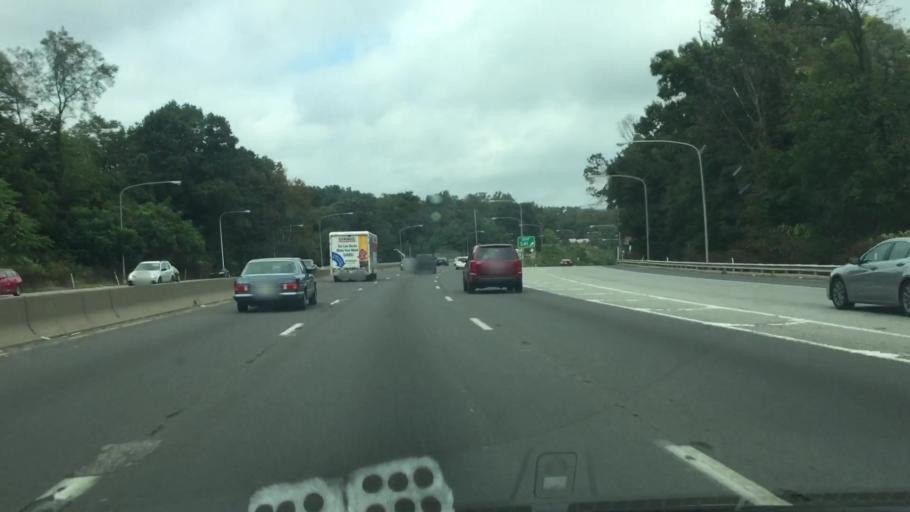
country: US
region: Pennsylvania
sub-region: Montgomery County
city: Bala-Cynwyd
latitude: 39.9843
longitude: -75.2082
